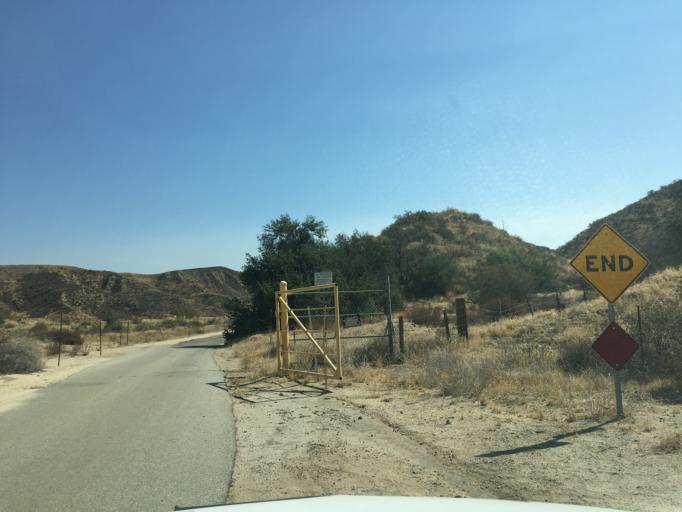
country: US
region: California
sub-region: Los Angeles County
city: Castaic
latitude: 34.4854
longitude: -118.6054
